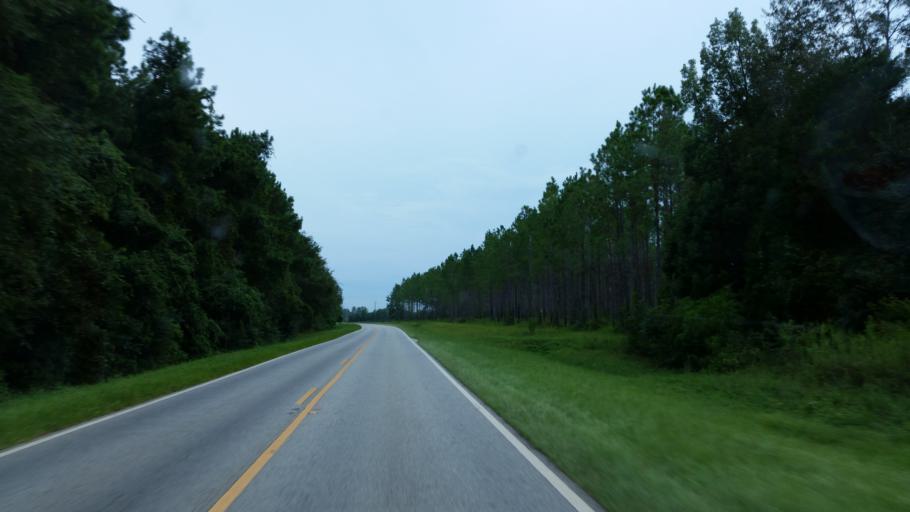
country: US
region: Georgia
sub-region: Lowndes County
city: Valdosta
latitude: 30.7471
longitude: -83.3104
